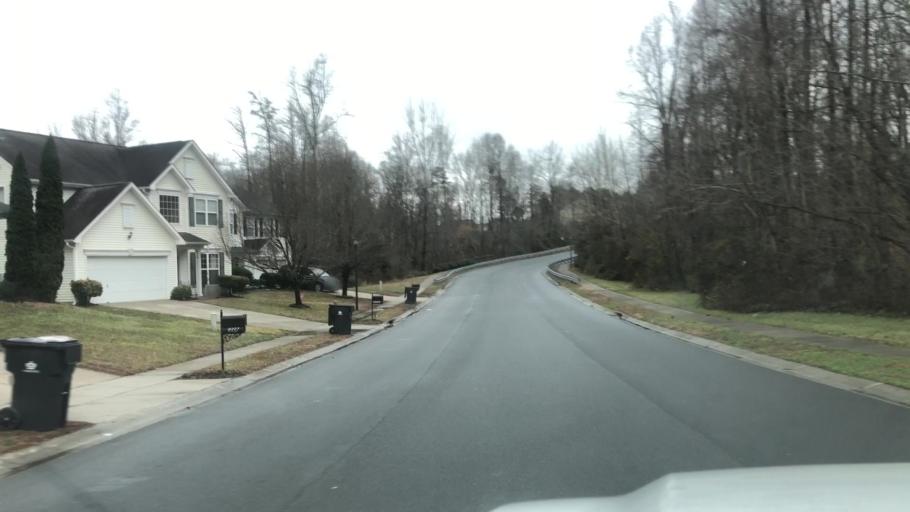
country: US
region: North Carolina
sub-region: Mecklenburg County
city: Mint Hill
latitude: 35.2411
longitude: -80.6827
